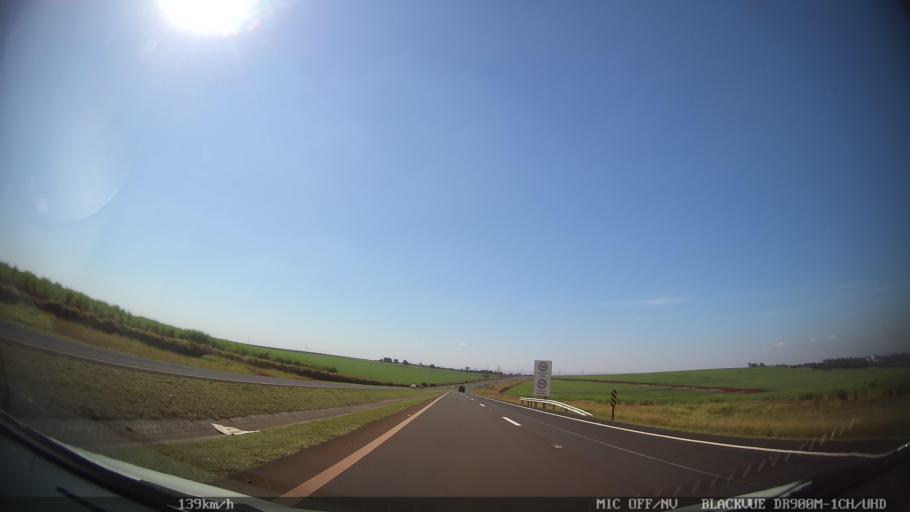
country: BR
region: Sao Paulo
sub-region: Ribeirao Preto
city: Ribeirao Preto
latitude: -21.1593
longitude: -47.8953
